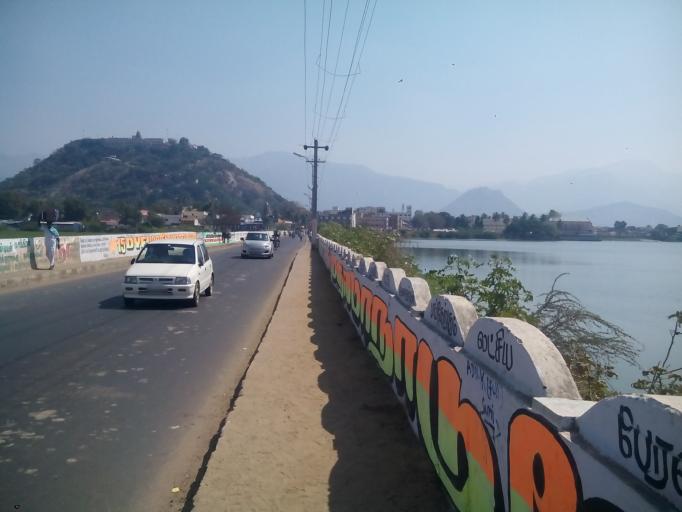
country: IN
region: Tamil Nadu
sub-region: Dindigul
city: Palani
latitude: 10.4479
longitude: 77.5149
